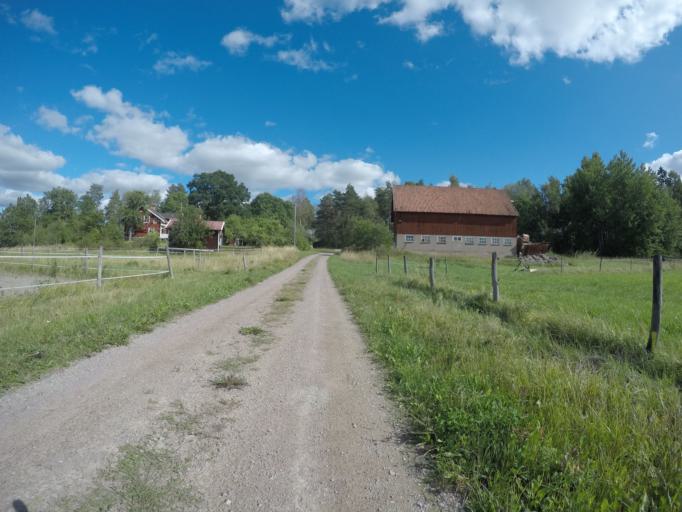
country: SE
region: Vaestmanland
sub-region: Hallstahammars Kommun
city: Kolback
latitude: 59.4971
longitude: 16.2030
